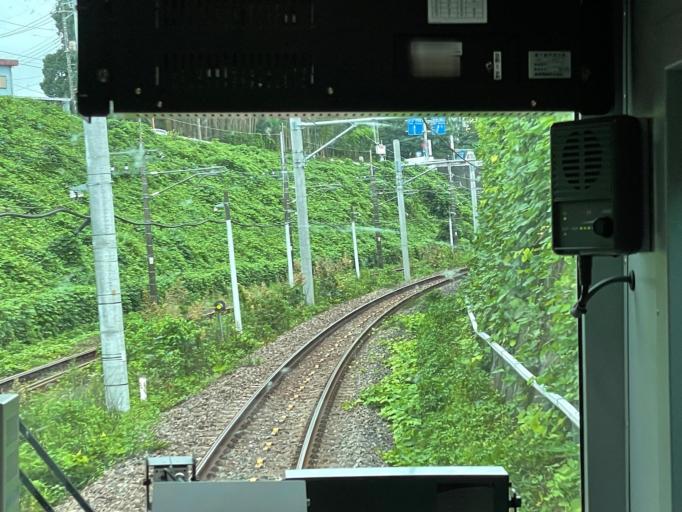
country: JP
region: Tochigi
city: Ujiie
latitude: 36.6125
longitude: 139.9771
